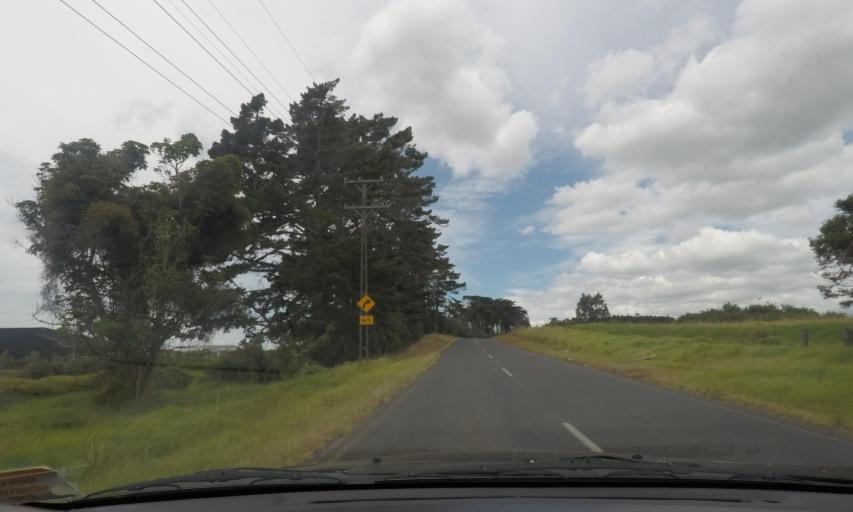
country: NZ
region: Auckland
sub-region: Auckland
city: Mangere
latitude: -36.9938
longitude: 174.7693
